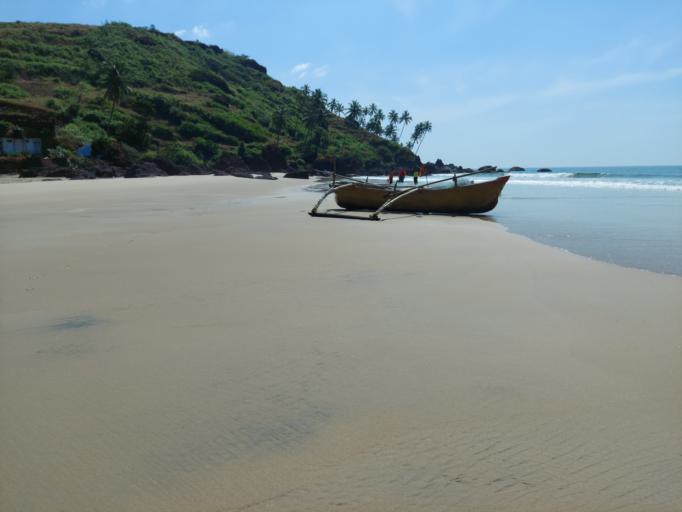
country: IN
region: Maharashtra
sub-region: Sindhudurg
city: Vengurla
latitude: 15.9187
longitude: 73.5672
